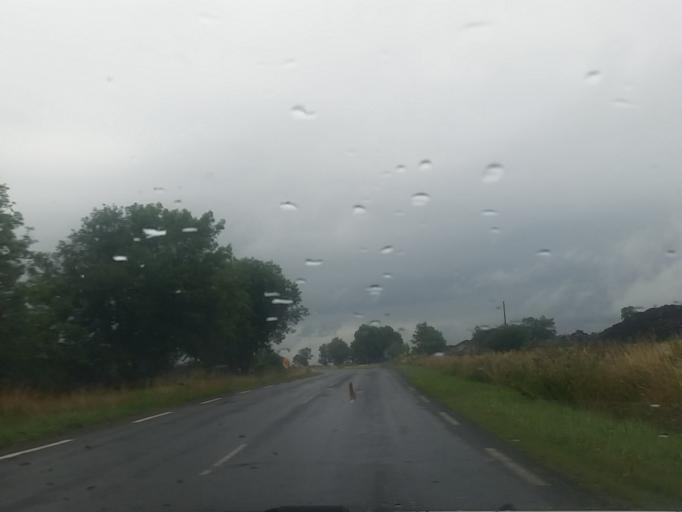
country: FR
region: Auvergne
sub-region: Departement du Cantal
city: Neuveglise
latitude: 44.9407
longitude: 3.0034
